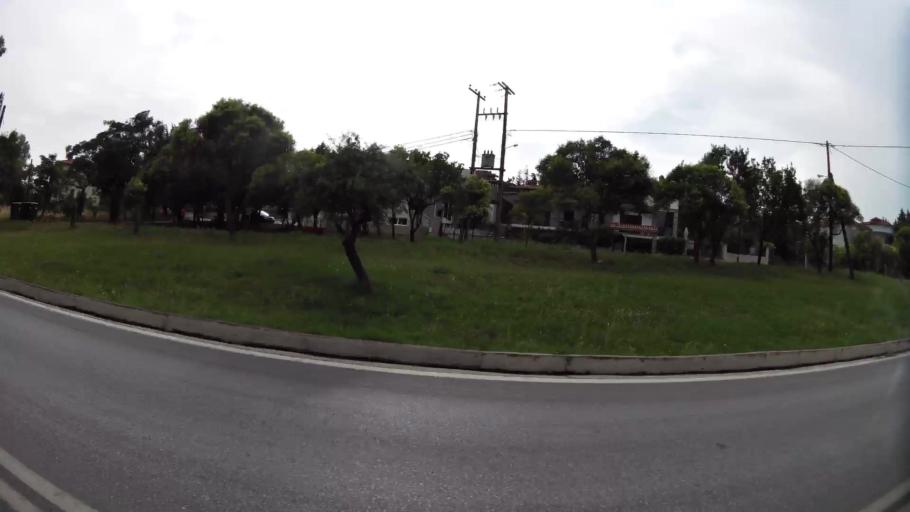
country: GR
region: Central Macedonia
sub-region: Nomos Thessalonikis
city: Oraiokastro
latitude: 40.7155
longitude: 22.9295
